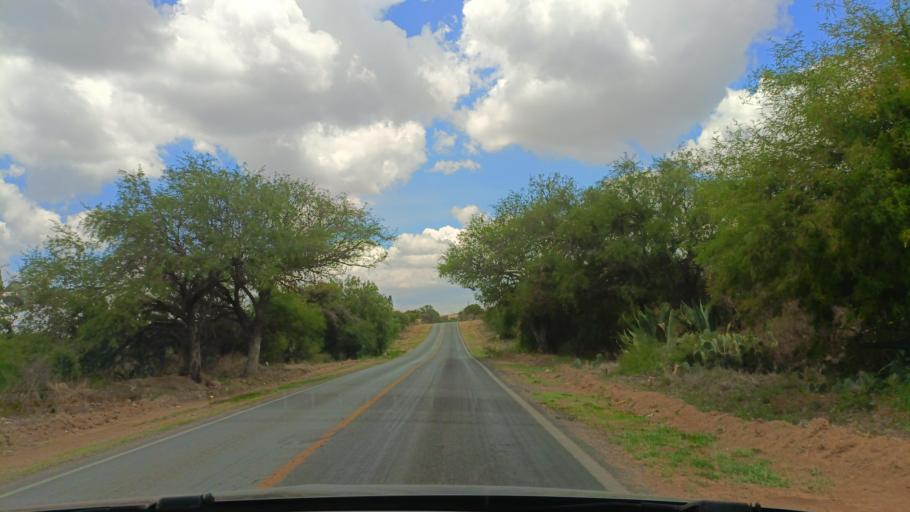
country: MX
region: Guanajuato
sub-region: San Luis de la Paz
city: San Ignacio
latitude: 21.2404
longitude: -100.4921
